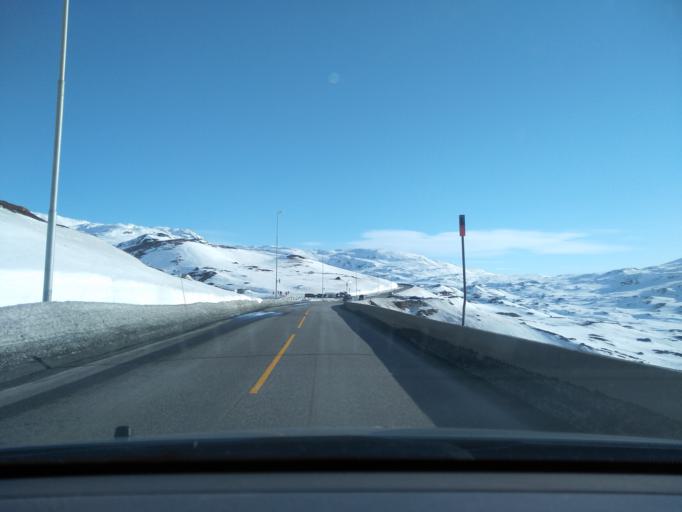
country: NO
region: Aust-Agder
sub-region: Bykle
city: Hovden
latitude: 59.8457
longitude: 6.9708
